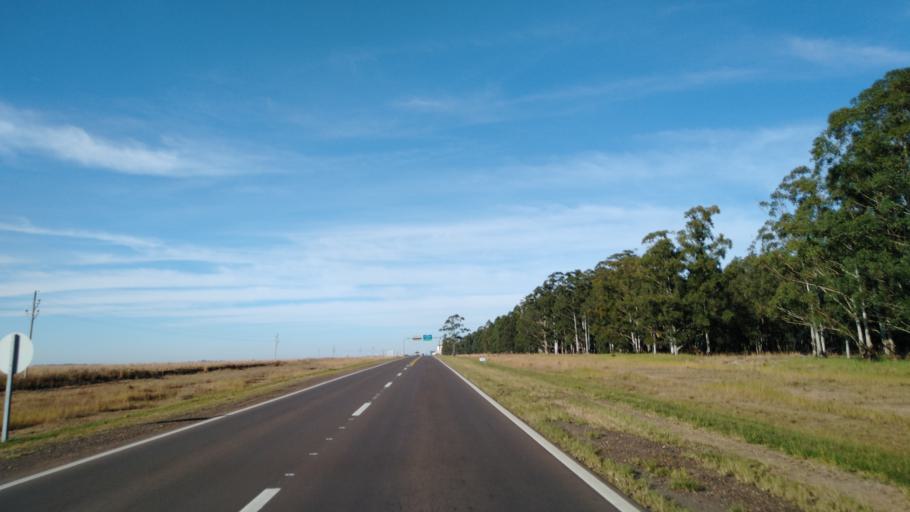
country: AR
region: Corrientes
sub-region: Departamento de Paso de los Libres
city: Paso de los Libres
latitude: -29.6982
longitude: -57.2122
